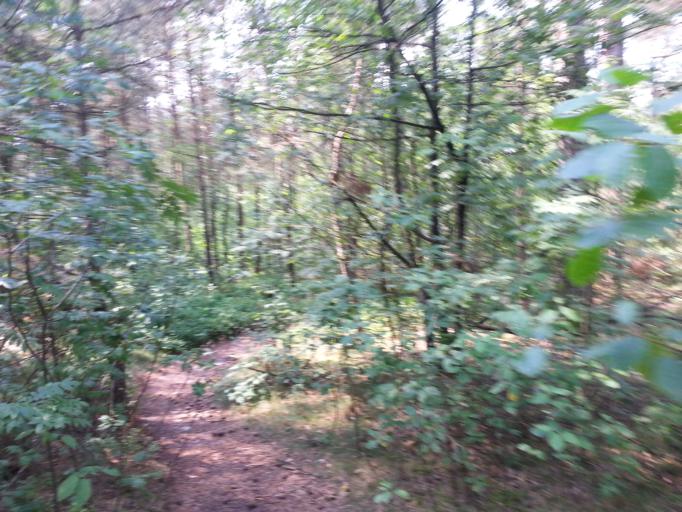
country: NL
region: Utrecht
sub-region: Gemeente Utrechtse Heuvelrug
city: Maarn
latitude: 52.1020
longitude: 5.3759
